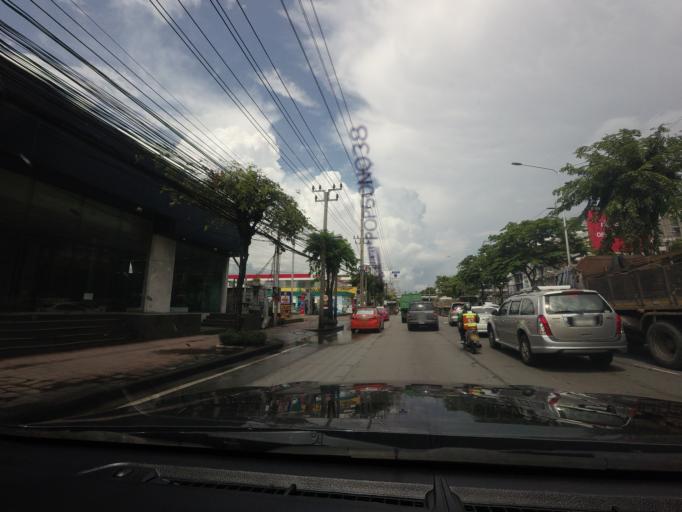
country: TH
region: Bangkok
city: Bang Khae
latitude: 13.7096
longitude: 100.3973
